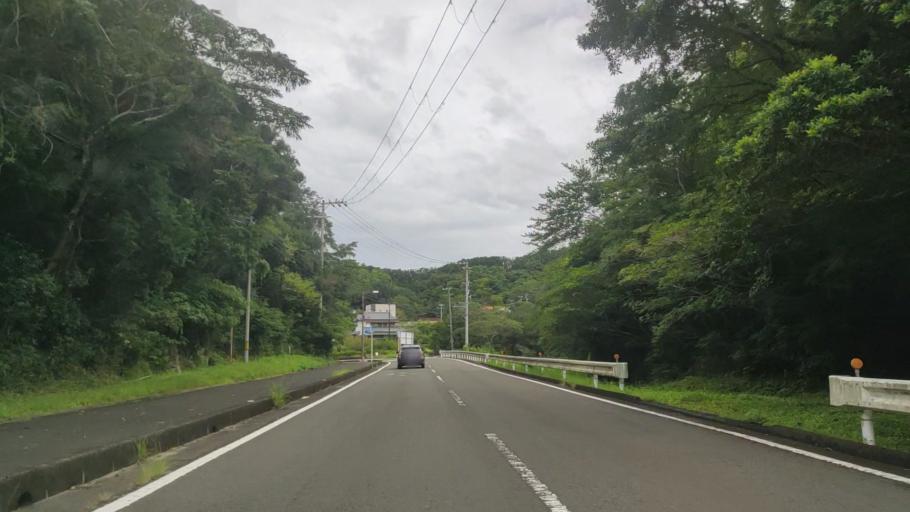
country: JP
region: Wakayama
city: Tanabe
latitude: 33.6817
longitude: 135.3887
